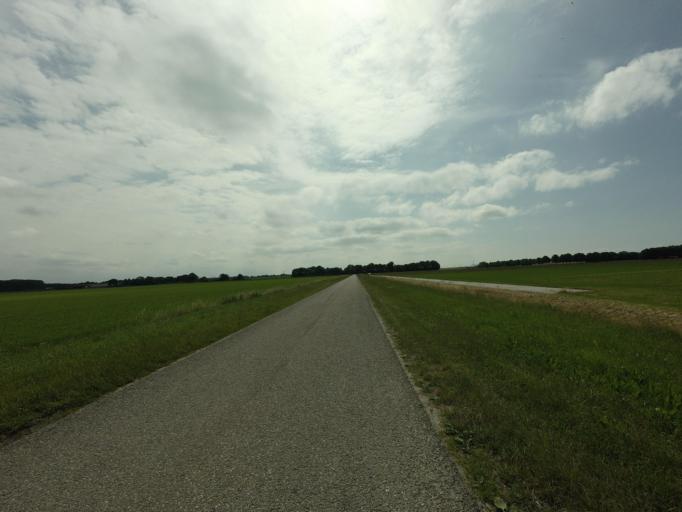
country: NL
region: Flevoland
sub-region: Gemeente Lelystad
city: Lelystad
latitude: 52.4314
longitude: 5.4851
